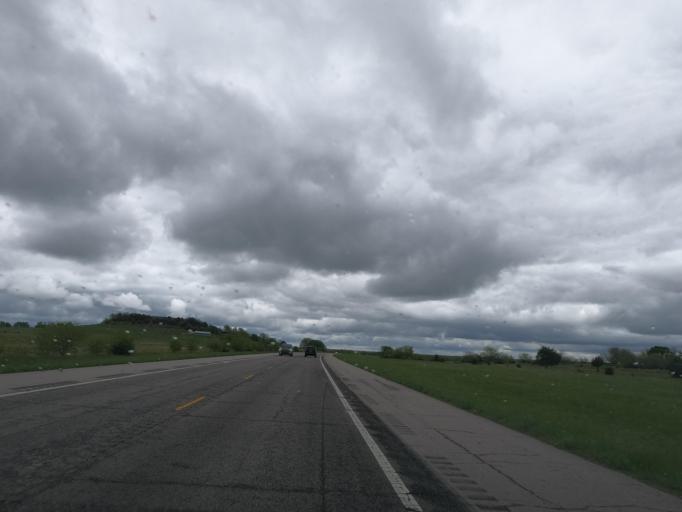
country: US
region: Kansas
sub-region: Montgomery County
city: Cherryvale
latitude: 37.3466
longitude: -95.4738
